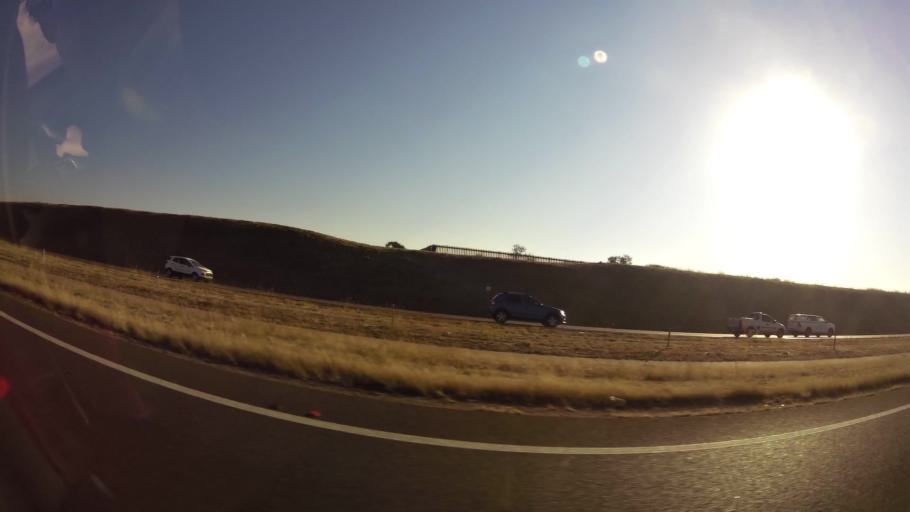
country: ZA
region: Gauteng
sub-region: City of Tshwane Metropolitan Municipality
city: Pretoria
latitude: -25.6413
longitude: 28.2255
